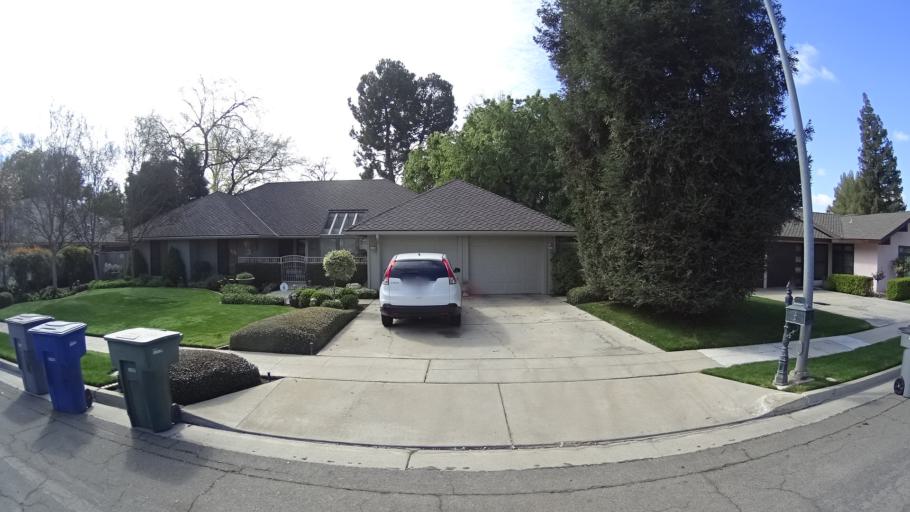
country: US
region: California
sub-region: Fresno County
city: Fresno
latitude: 36.8337
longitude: -119.8530
